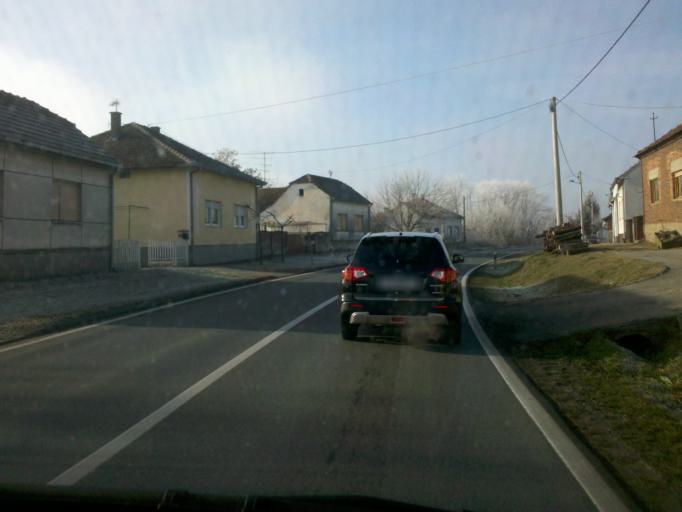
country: HR
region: Virovitick-Podravska
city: Pitomaca
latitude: 45.9643
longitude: 17.2148
